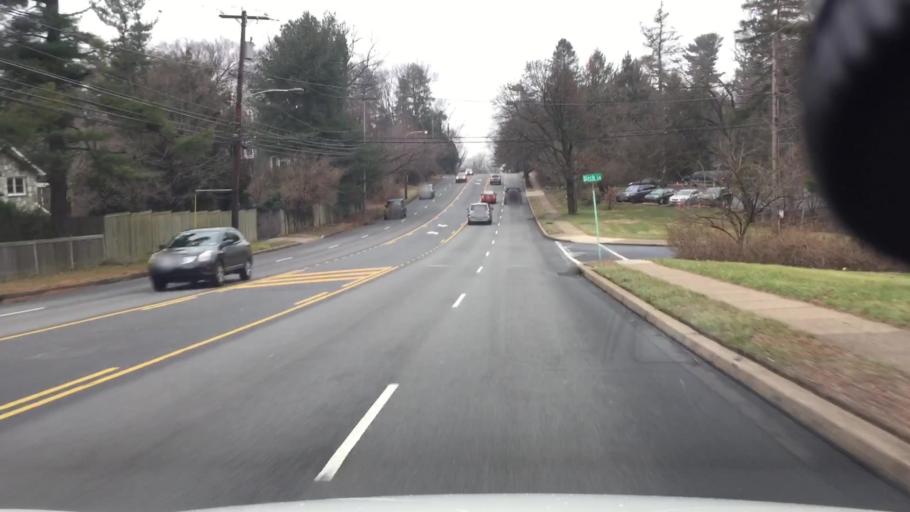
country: US
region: Pennsylvania
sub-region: Montgomery County
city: Wyndmoor
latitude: 40.0821
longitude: -75.2045
